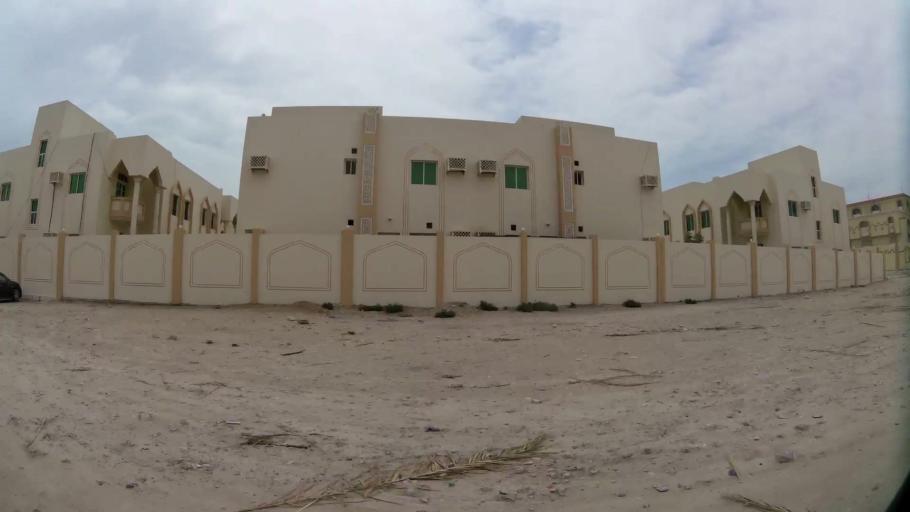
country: QA
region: Baladiyat ar Rayyan
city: Ar Rayyan
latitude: 25.2312
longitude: 51.4530
